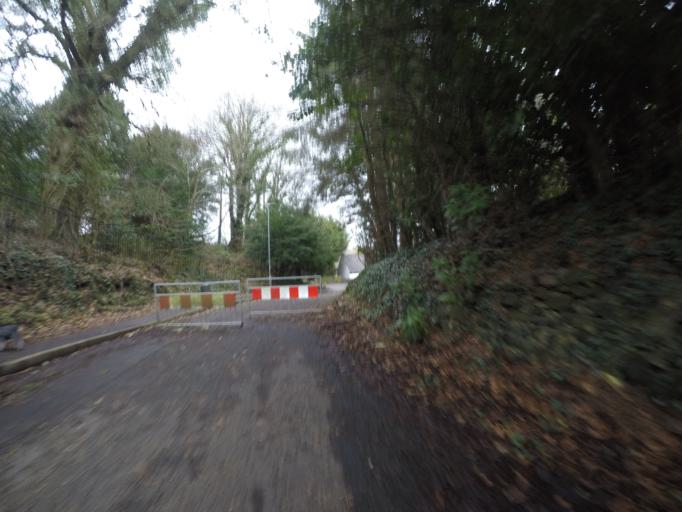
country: GB
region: Scotland
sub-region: North Ayrshire
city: Springside
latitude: 55.6307
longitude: -4.6200
